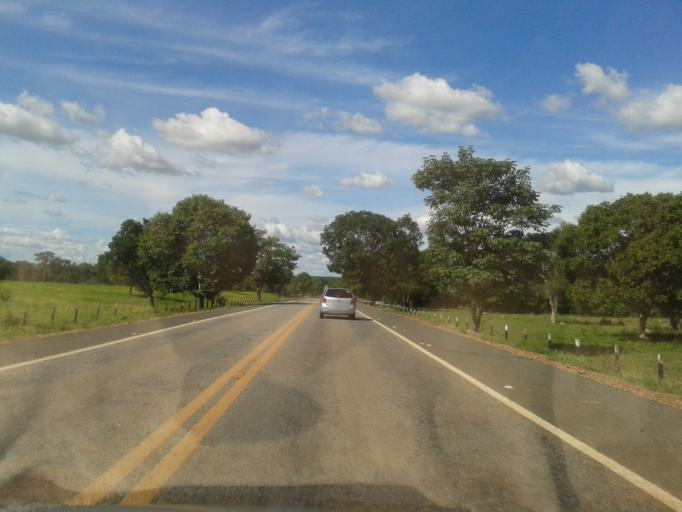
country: BR
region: Goias
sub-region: Mozarlandia
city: Mozarlandia
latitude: -15.0069
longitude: -50.5916
